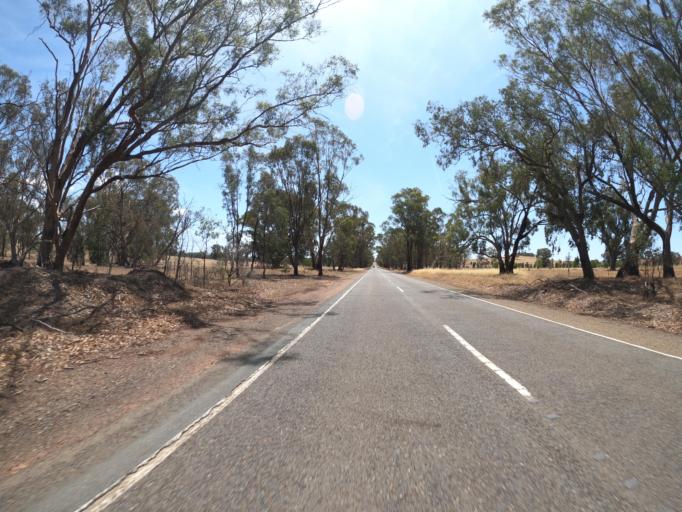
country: AU
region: Victoria
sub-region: Benalla
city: Benalla
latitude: -36.3595
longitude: 145.9669
